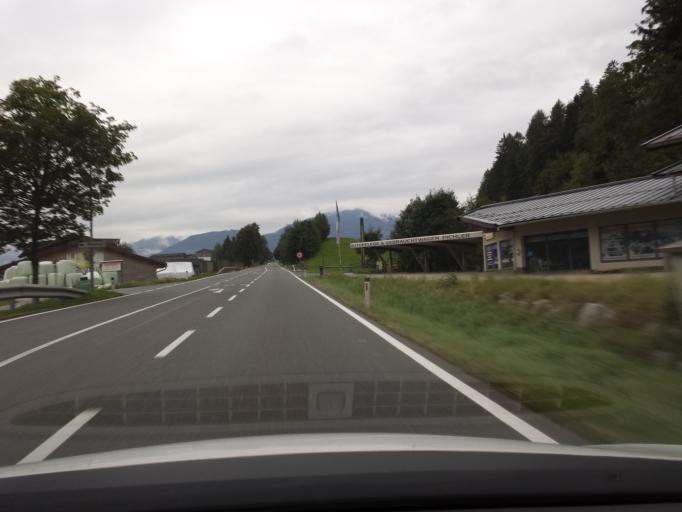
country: AT
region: Salzburg
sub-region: Politischer Bezirk Zell am See
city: Saalfelden am Steinernen Meer
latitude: 47.4514
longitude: 12.8336
